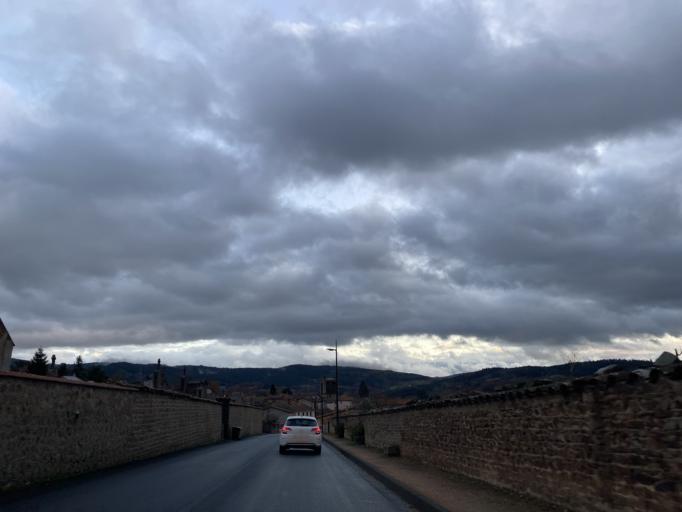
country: FR
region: Auvergne
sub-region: Departement du Puy-de-Dome
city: Cunlhat
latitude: 45.6352
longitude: 3.5591
